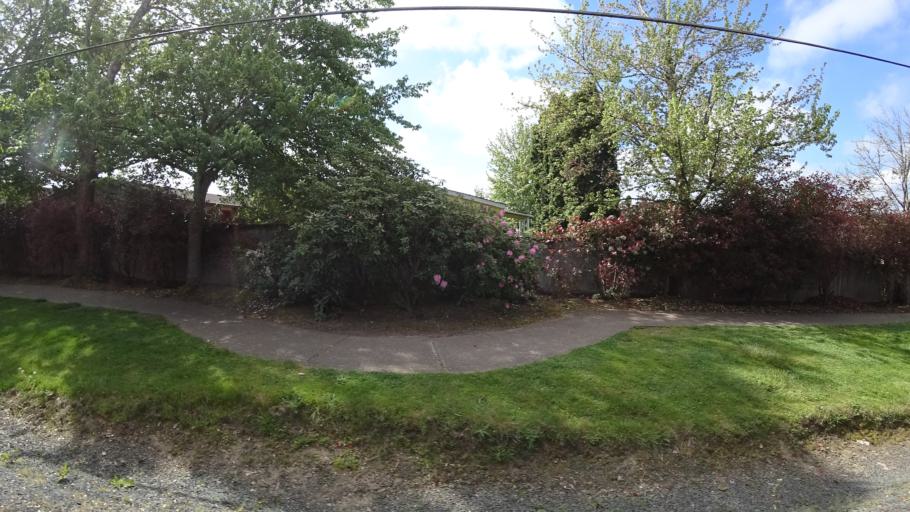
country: US
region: Oregon
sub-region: Washington County
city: Rockcreek
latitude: 45.5231
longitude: -122.8935
